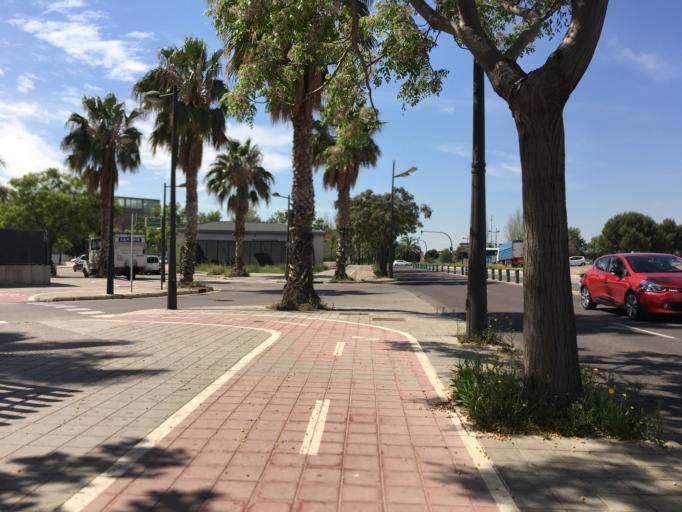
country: ES
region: Valencia
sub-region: Provincia de Valencia
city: Mislata
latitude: 39.4826
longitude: -0.4064
